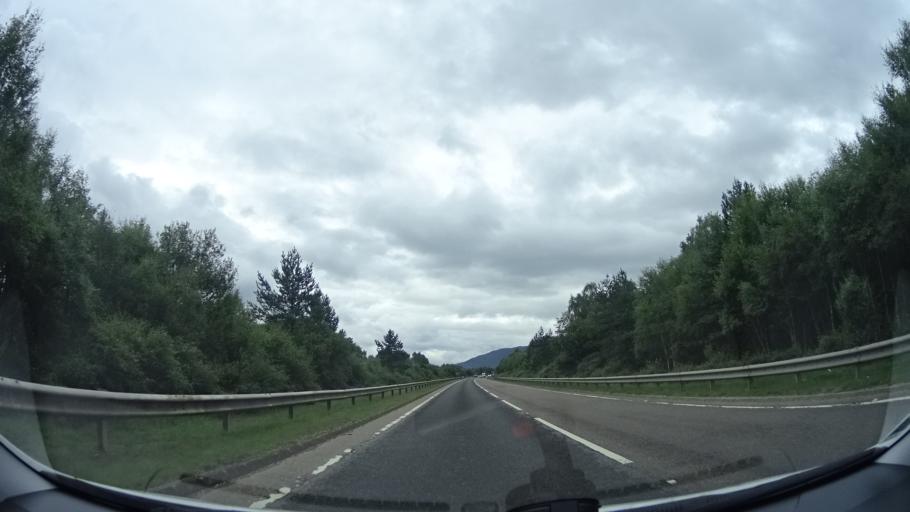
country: GB
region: Scotland
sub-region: Highland
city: Aviemore
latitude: 57.2186
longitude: -3.8216
